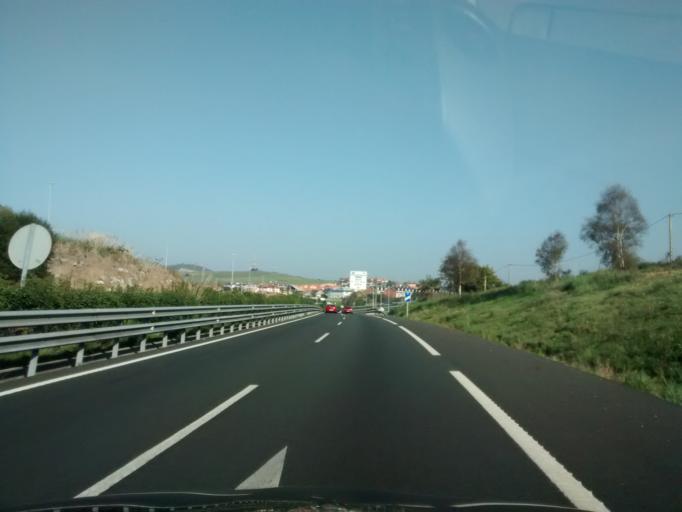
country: ES
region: Cantabria
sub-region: Provincia de Cantabria
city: Santa Cruz de Bezana
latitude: 43.4225
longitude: -3.9477
